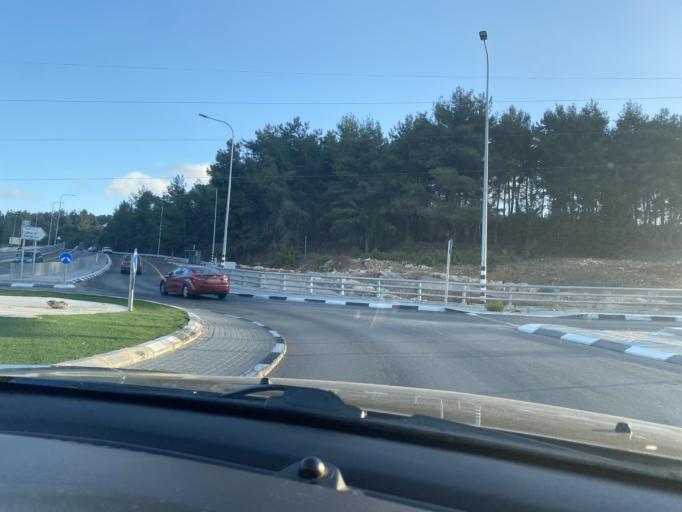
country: IL
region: Northern District
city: Kefar Weradim
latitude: 33.0013
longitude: 35.2821
